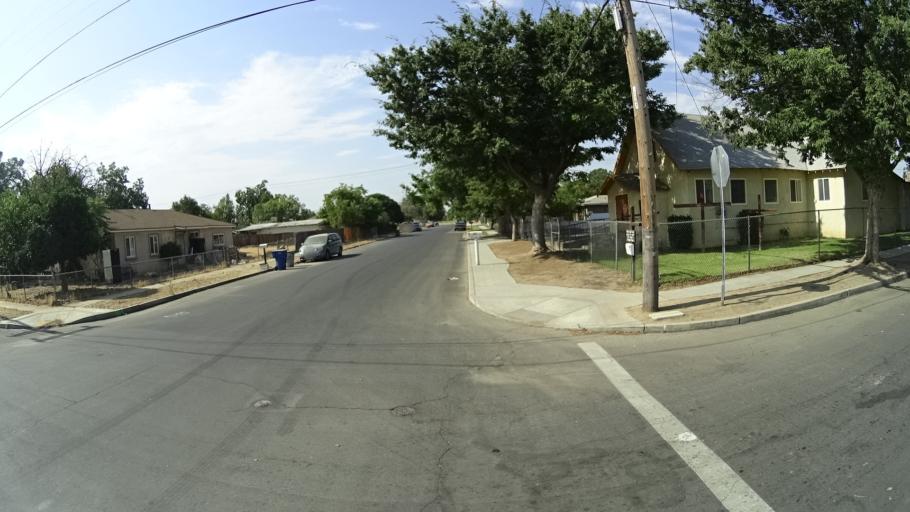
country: US
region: California
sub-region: Fresno County
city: West Park
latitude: 36.7196
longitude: -119.8134
